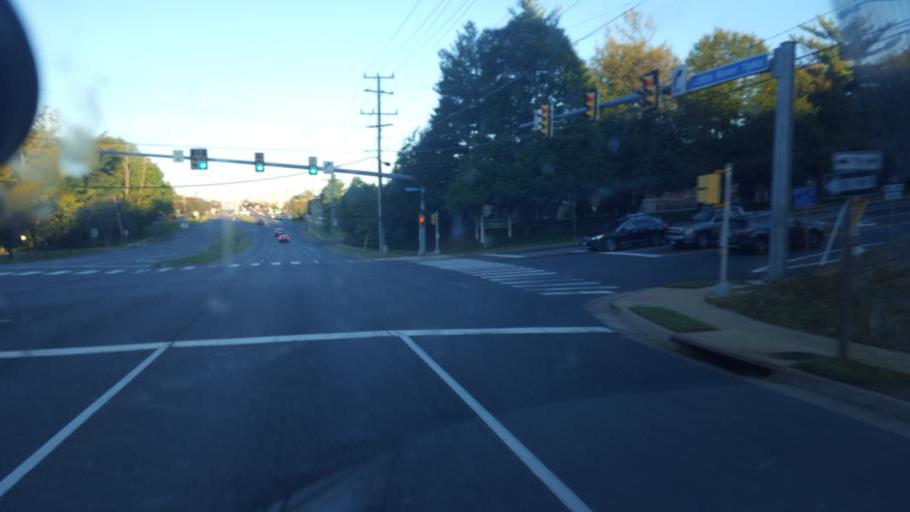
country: US
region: Virginia
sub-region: Fairfax County
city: Annandale
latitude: 38.8286
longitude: -77.1851
